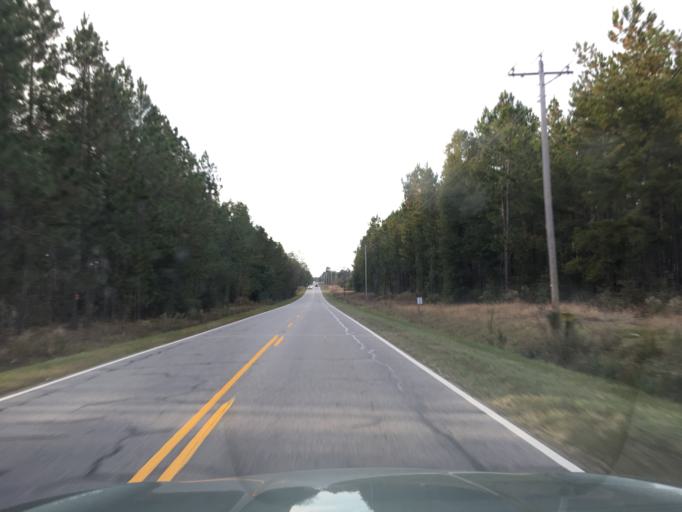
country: US
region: South Carolina
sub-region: Lexington County
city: Leesville
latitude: 33.7891
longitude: -81.4165
